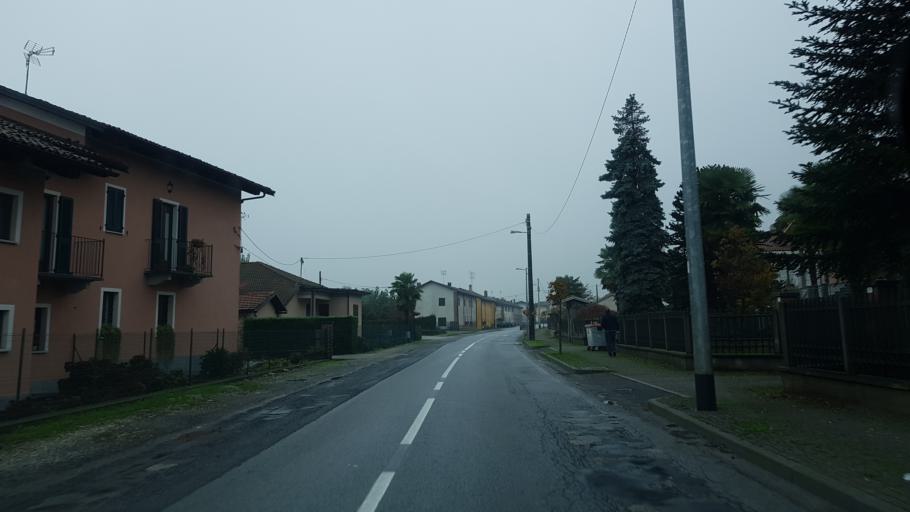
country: IT
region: Piedmont
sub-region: Provincia di Cuneo
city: Vottignasco
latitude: 44.5645
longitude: 7.5821
